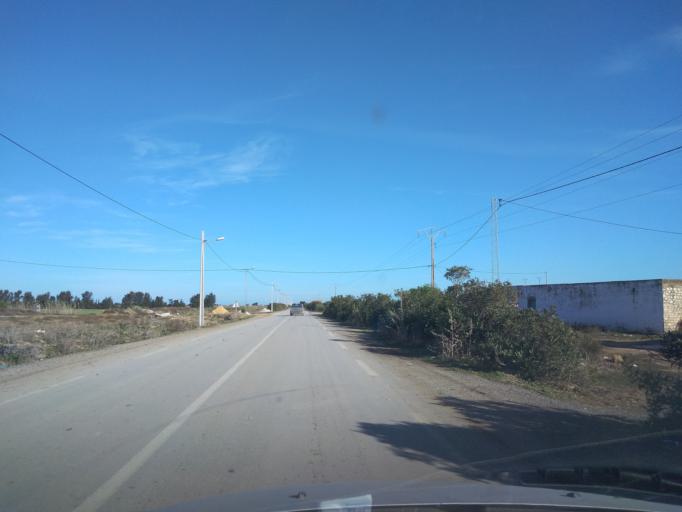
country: TN
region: Ariana
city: Qal'at al Andalus
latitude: 37.0612
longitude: 10.1327
